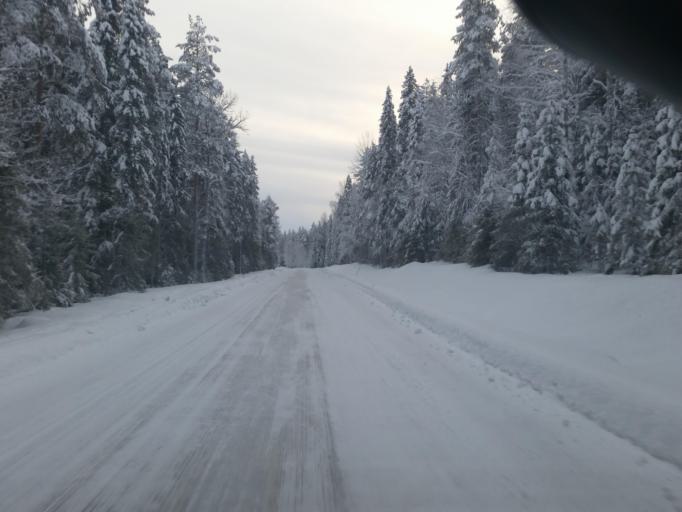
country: SE
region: Norrbotten
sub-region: Pitea Kommun
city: Norrfjarden
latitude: 65.5895
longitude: 21.4603
